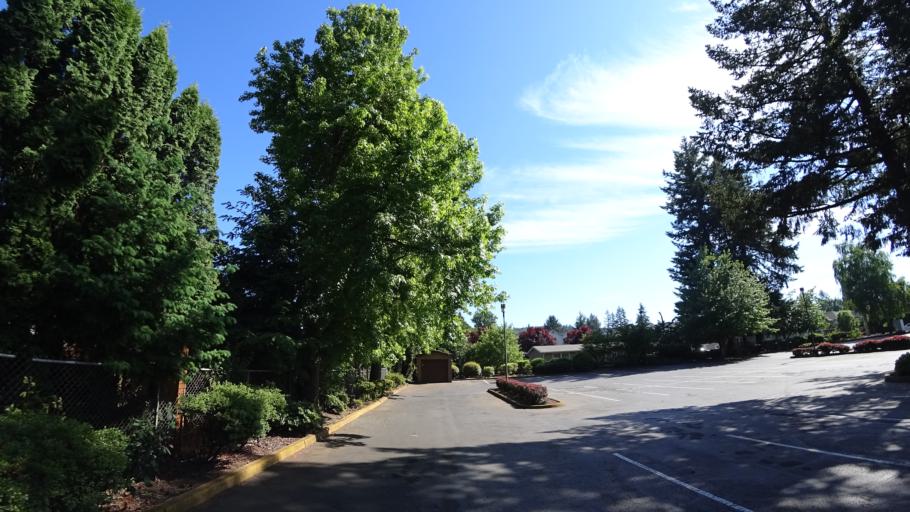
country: US
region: Oregon
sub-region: Multnomah County
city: Gresham
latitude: 45.4958
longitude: -122.4745
